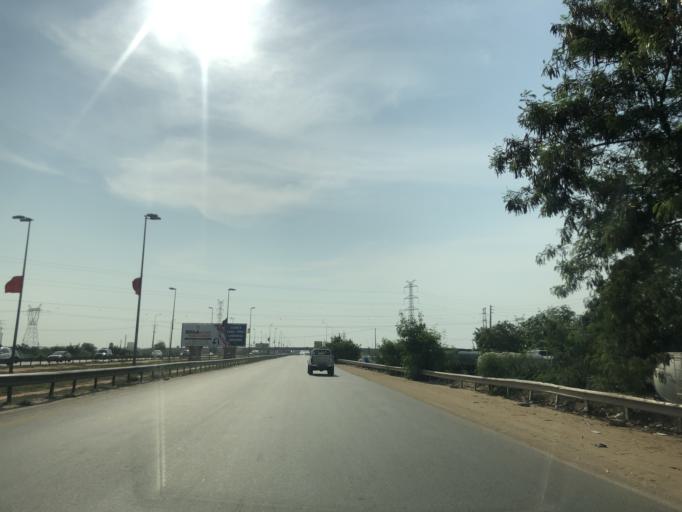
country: AO
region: Luanda
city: Luanda
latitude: -8.9732
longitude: 13.2600
